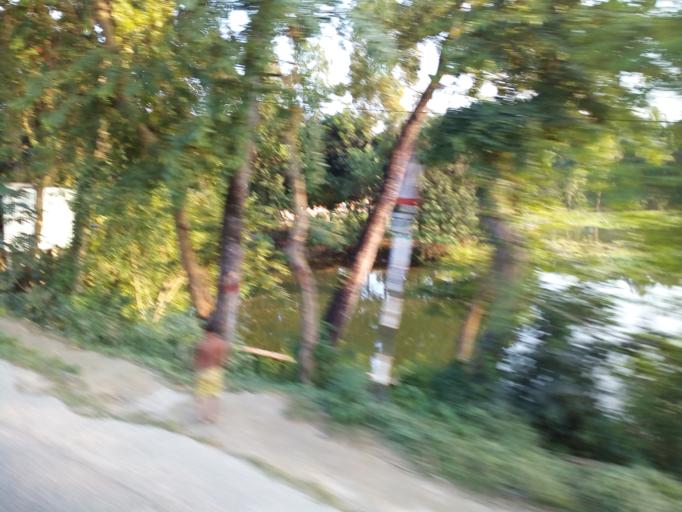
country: BD
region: Dhaka
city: Nagarpur
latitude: 23.8486
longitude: 89.8866
